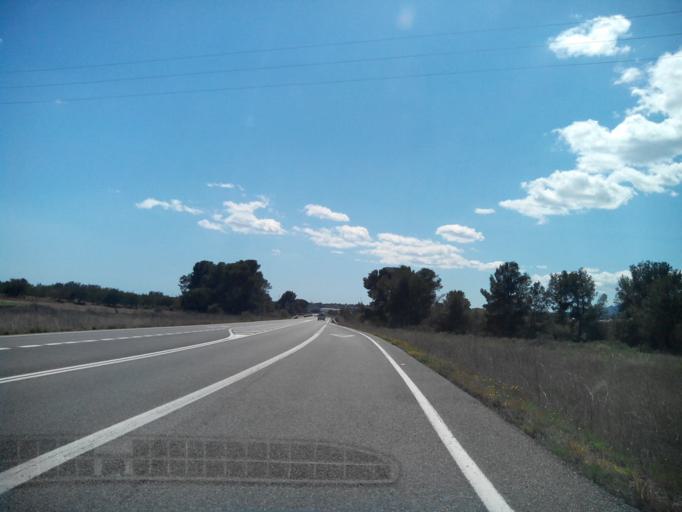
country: ES
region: Catalonia
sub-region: Provincia de Tarragona
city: Riudecanyes
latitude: 41.0968
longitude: 0.9735
